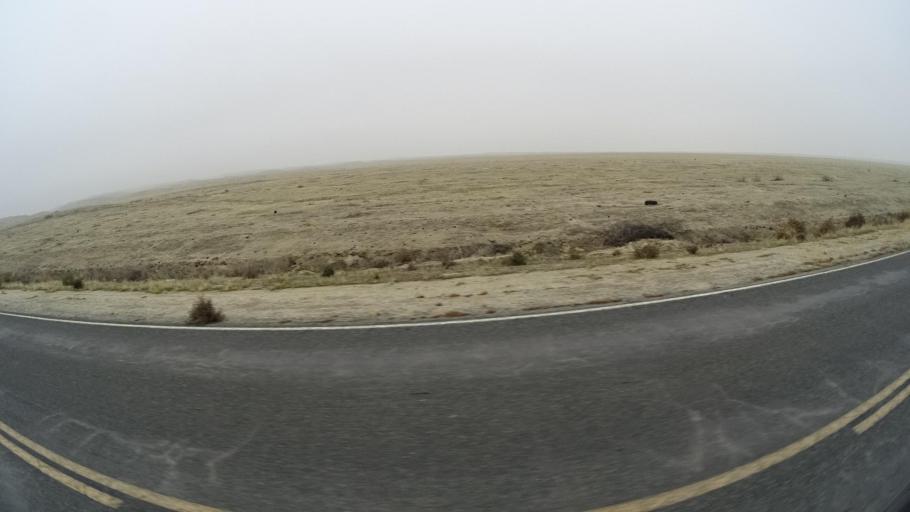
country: US
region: California
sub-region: Kern County
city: Buttonwillow
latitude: 35.3343
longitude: -119.4636
